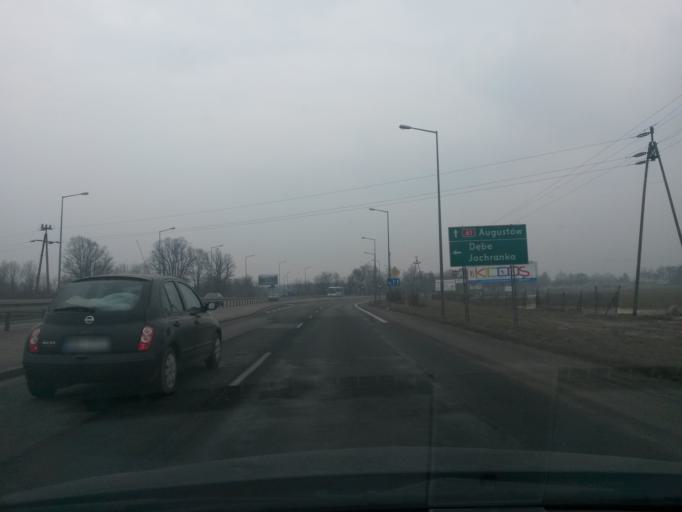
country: PL
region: Masovian Voivodeship
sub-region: Powiat legionowski
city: Bialobrzegi
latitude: 52.4700
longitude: 21.0295
